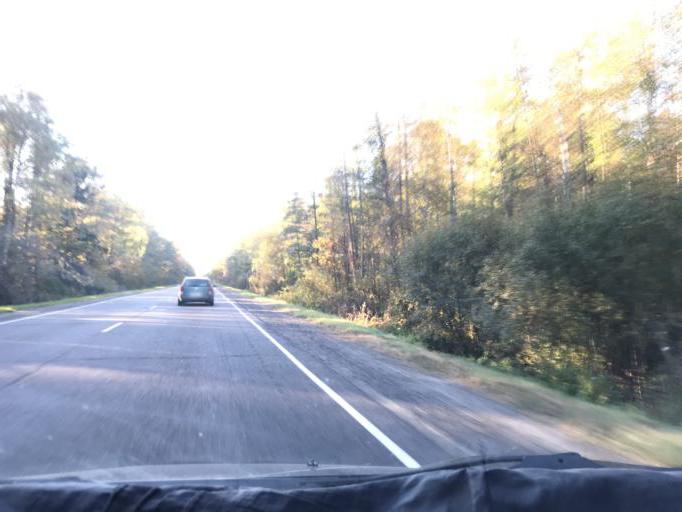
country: BY
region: Gomel
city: Pyetrykaw
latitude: 52.2688
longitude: 28.2869
